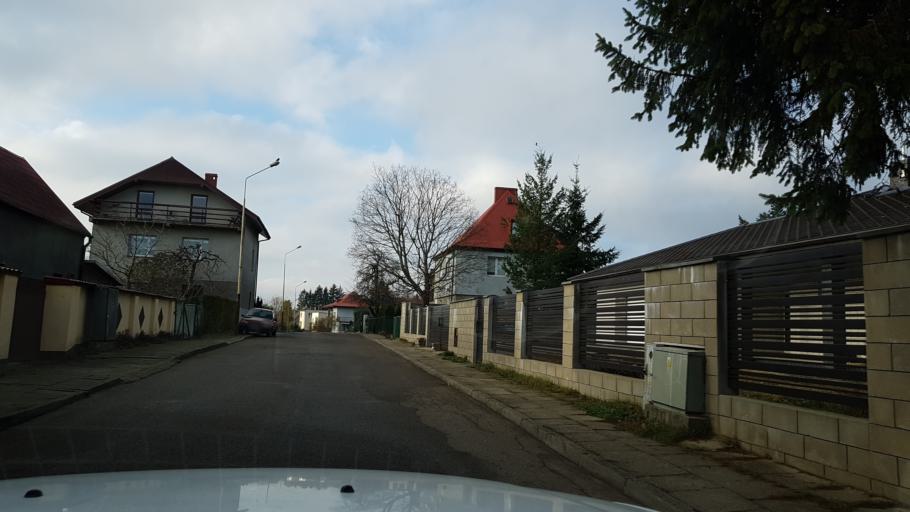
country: PL
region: West Pomeranian Voivodeship
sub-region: Powiat stargardzki
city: Insko
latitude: 53.4389
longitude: 15.5416
